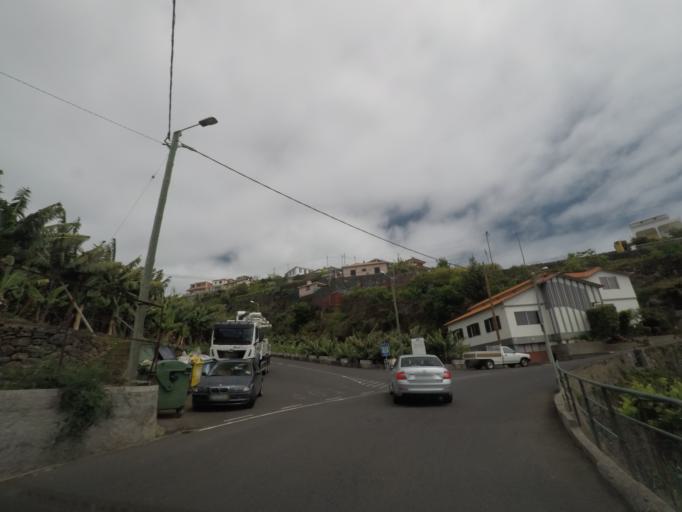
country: PT
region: Madeira
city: Ponta do Sol
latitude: 32.6865
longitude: -17.1035
